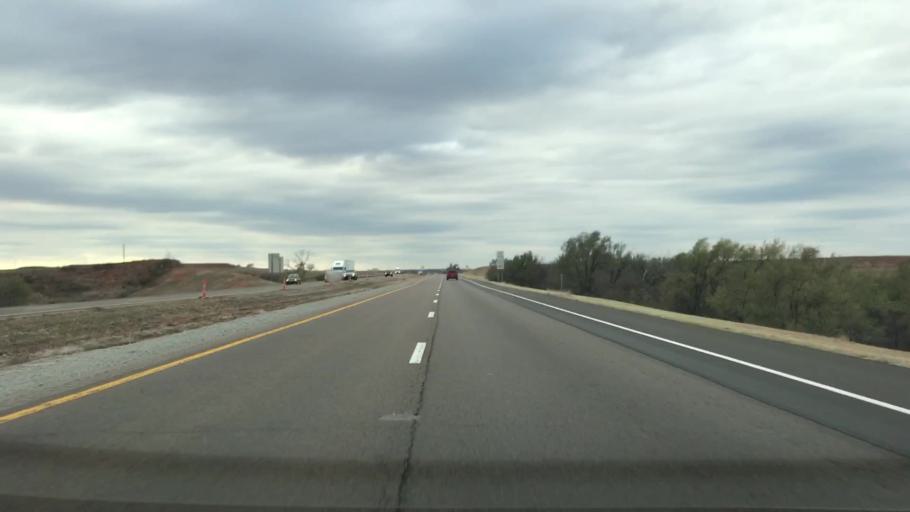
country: US
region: Oklahoma
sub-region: Washita County
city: Burns Flat
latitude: 35.4414
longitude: -99.1802
